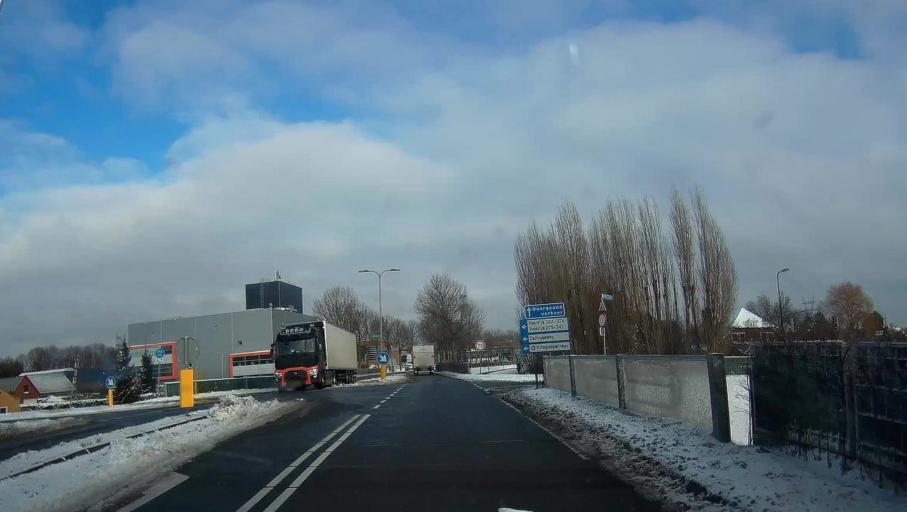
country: NL
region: South Holland
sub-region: Gemeente Barendrecht
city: Barendrecht
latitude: 51.8585
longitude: 4.5189
